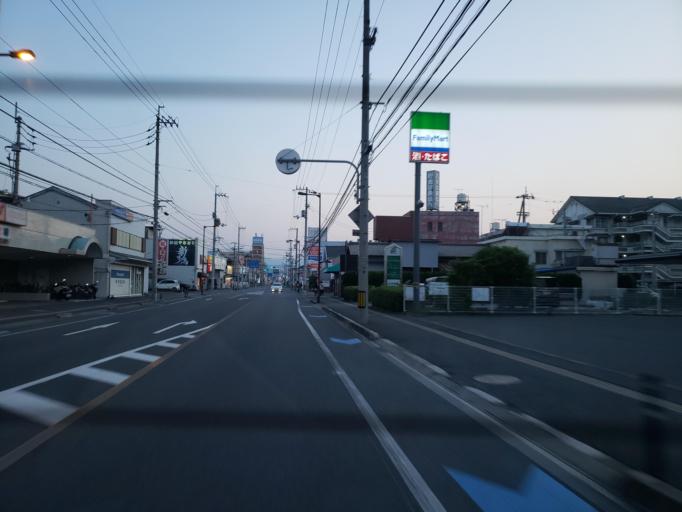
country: JP
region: Ehime
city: Hojo
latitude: 34.0540
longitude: 132.9864
